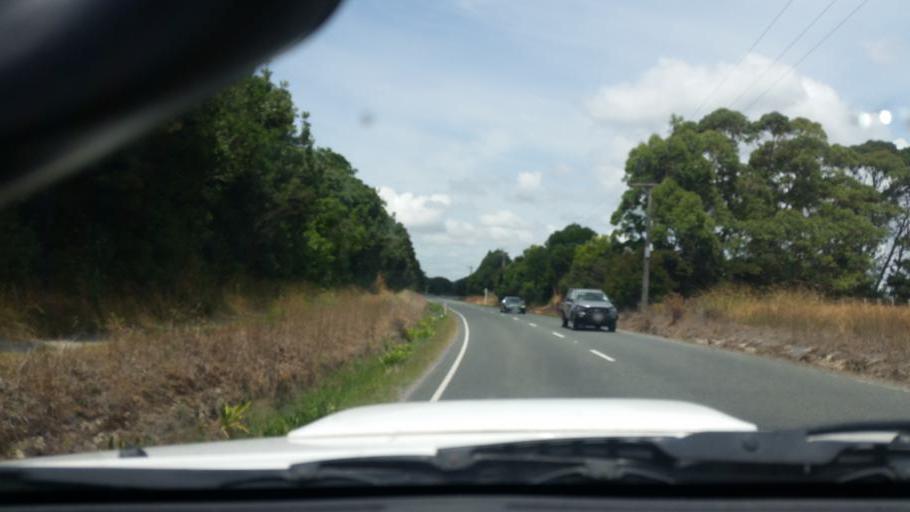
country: NZ
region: Auckland
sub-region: Auckland
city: Wellsford
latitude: -36.1131
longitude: 174.5751
